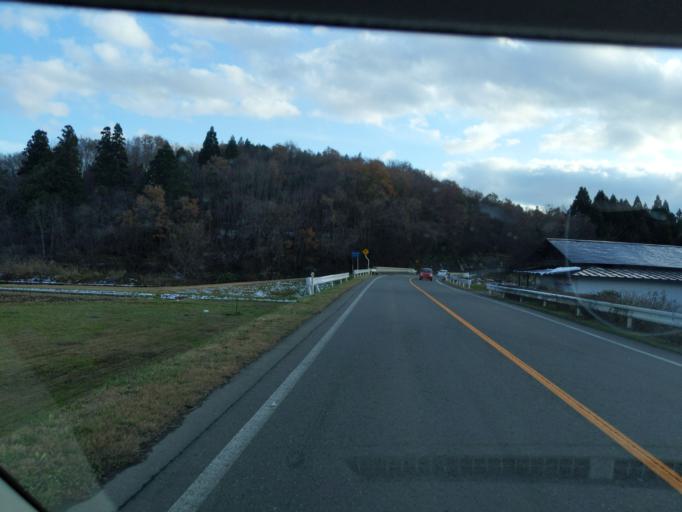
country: JP
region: Iwate
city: Mizusawa
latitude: 39.1869
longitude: 141.0534
